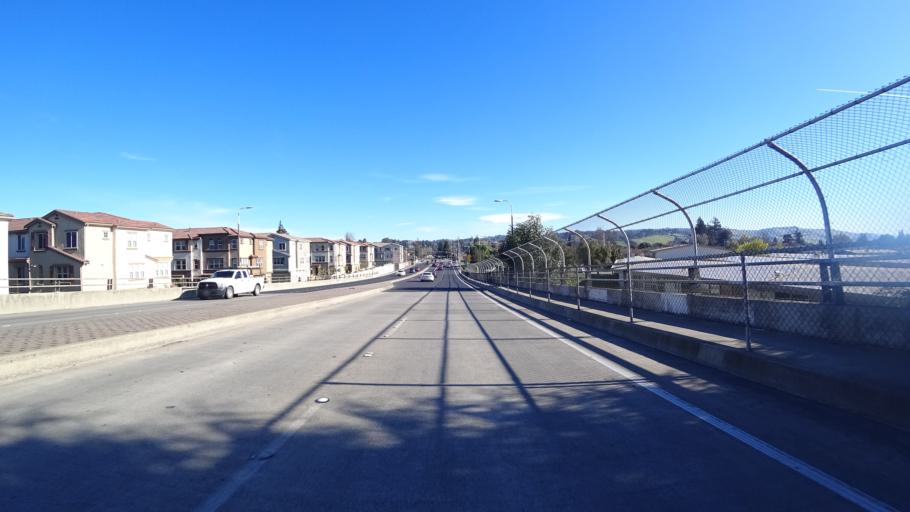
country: US
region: California
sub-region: Alameda County
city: Hayward
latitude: 37.6603
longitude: -122.0912
